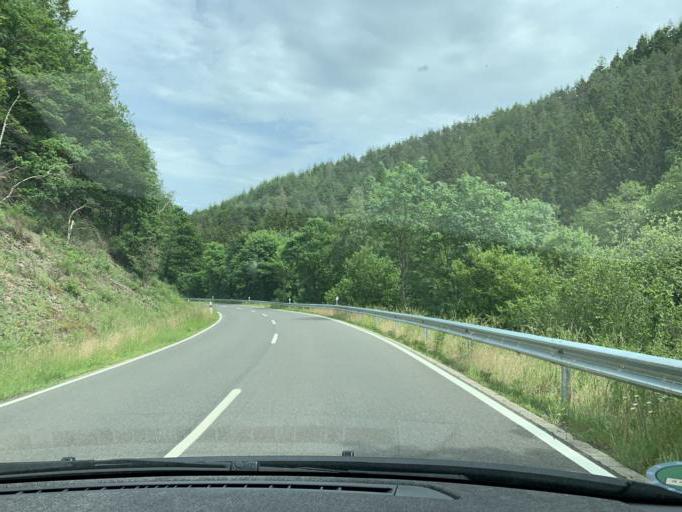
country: DE
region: North Rhine-Westphalia
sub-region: Regierungsbezirk Koln
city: Hurtgenwald
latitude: 50.6859
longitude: 6.4003
